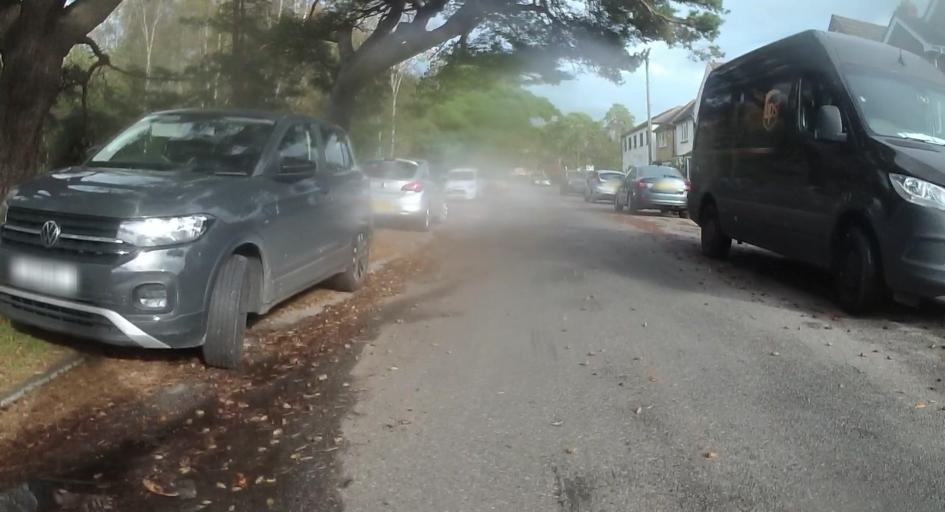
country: GB
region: England
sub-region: Surrey
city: Frimley
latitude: 51.3099
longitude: -0.7047
